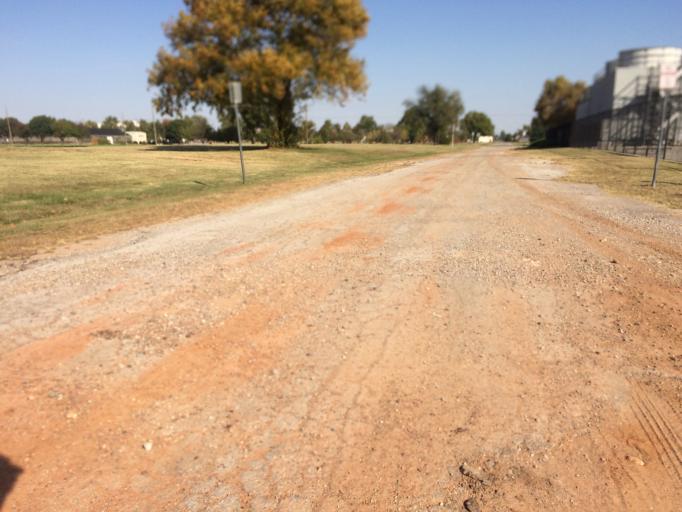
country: US
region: Oklahoma
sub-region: Cleveland County
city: Norman
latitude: 35.1860
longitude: -97.4370
